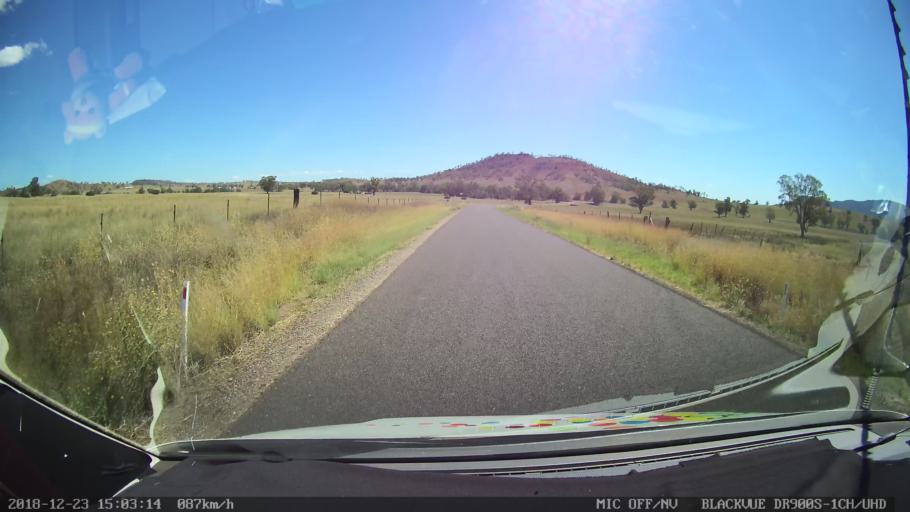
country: AU
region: New South Wales
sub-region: Tamworth Municipality
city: Manilla
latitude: -30.7367
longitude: 150.7671
